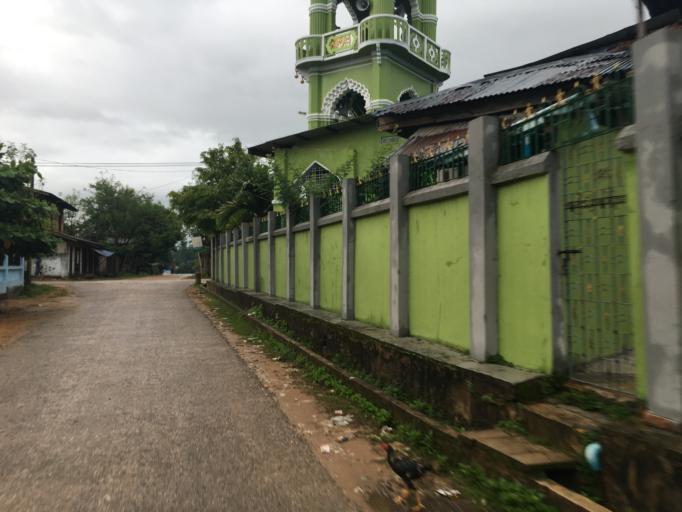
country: MM
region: Mon
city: Mudon
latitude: 16.0405
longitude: 98.1186
